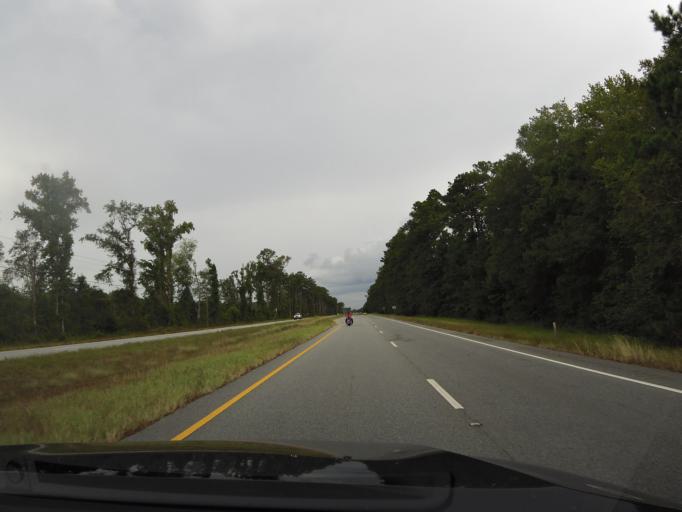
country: US
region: Georgia
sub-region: McIntosh County
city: Darien
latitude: 31.3561
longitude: -81.6139
